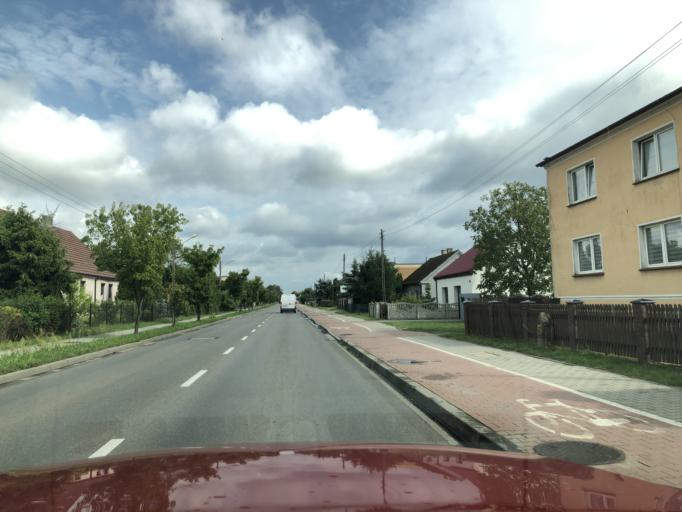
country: PL
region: Greater Poland Voivodeship
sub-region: Powiat szamotulski
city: Pniewy
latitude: 52.5164
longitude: 16.2612
